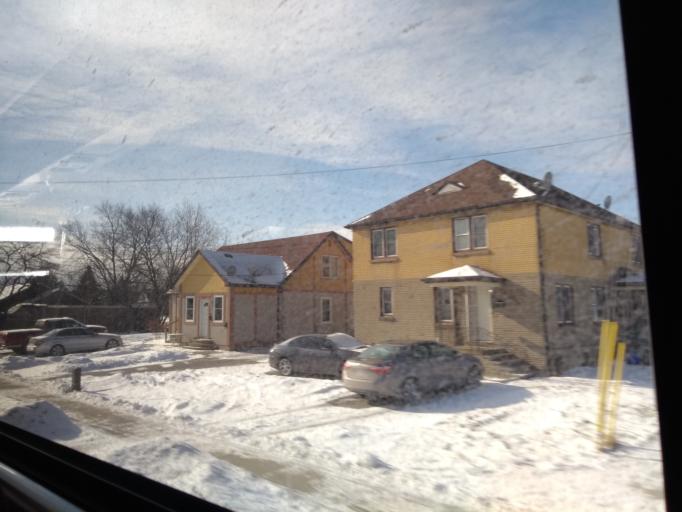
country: CA
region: Ontario
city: Niagara Falls
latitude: 43.1022
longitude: -79.0857
